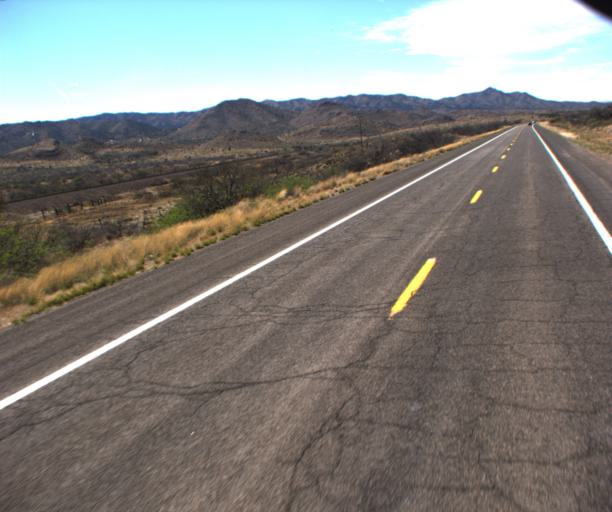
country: US
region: Arizona
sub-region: Mohave County
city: Peach Springs
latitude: 35.3628
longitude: -113.6993
